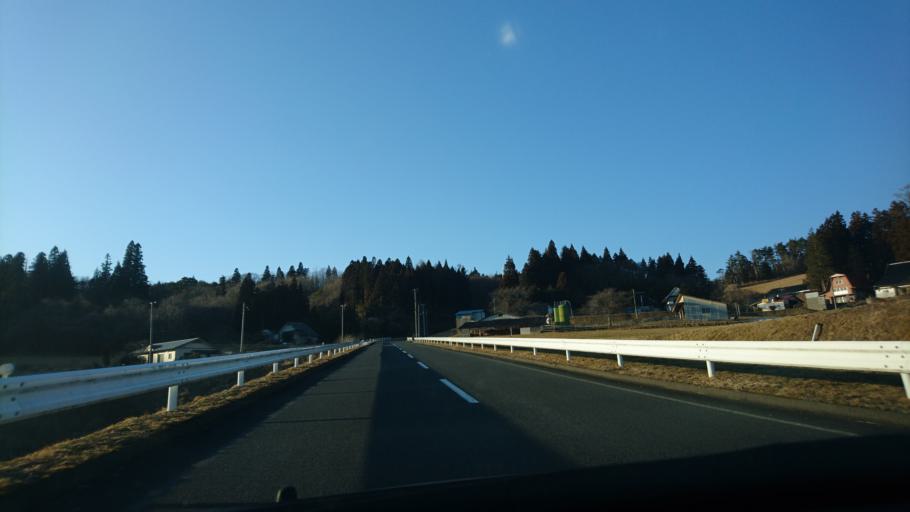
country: JP
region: Iwate
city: Mizusawa
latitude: 39.0264
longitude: 141.3748
